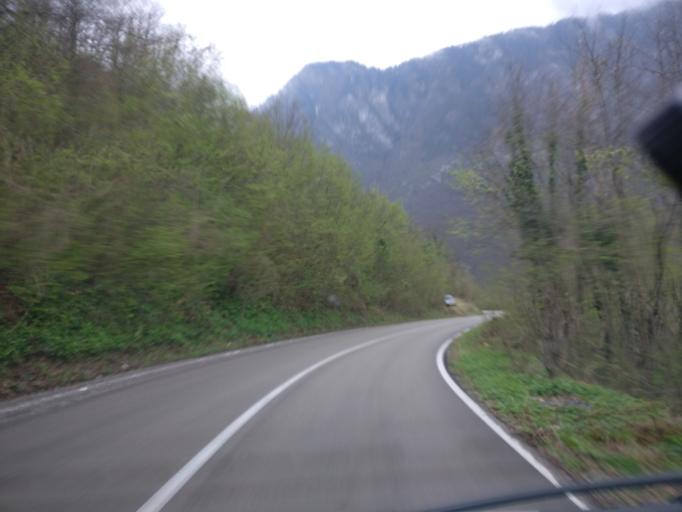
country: ME
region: Opstina Pluzine
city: Pluzine
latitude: 43.3115
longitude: 18.8547
